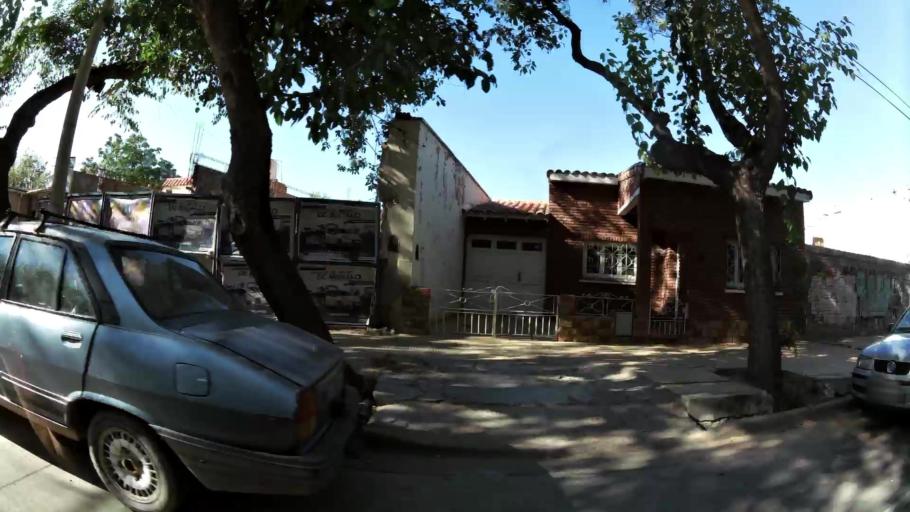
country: AR
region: Mendoza
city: Las Heras
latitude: -32.8685
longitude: -68.8452
